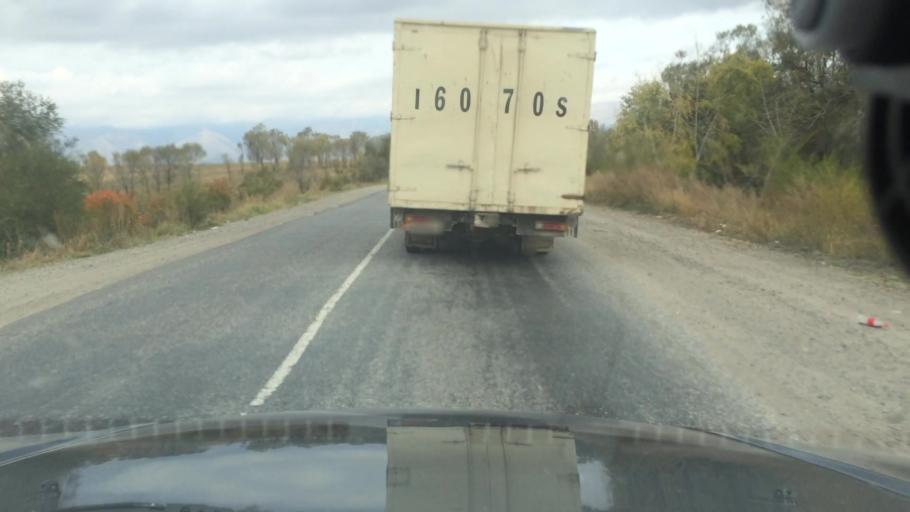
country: KG
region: Ysyk-Koel
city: Tyup
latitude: 42.6673
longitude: 78.3490
